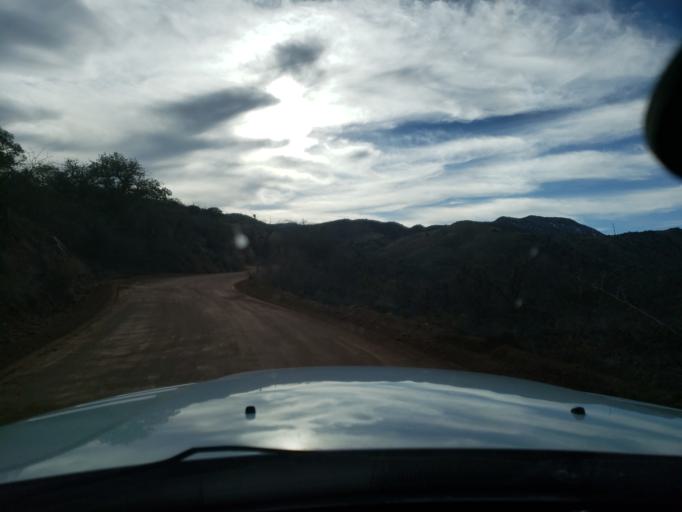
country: US
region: Arizona
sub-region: Pinal County
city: Oracle
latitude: 32.5490
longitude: -110.7072
